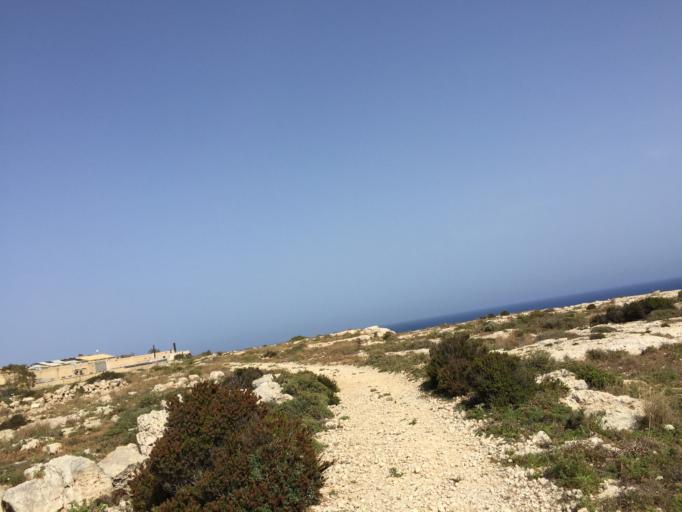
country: MT
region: Birzebbuga
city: Birzebbuga
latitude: 35.8073
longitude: 14.5122
